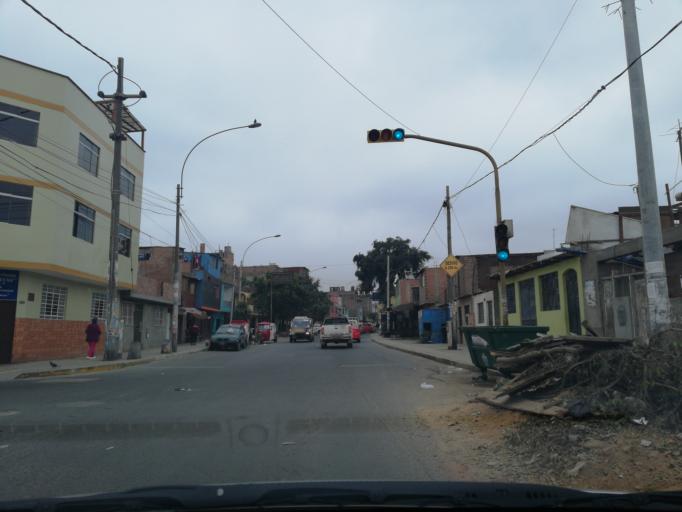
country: PE
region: Lima
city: Lima
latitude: -12.0375
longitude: -77.0500
